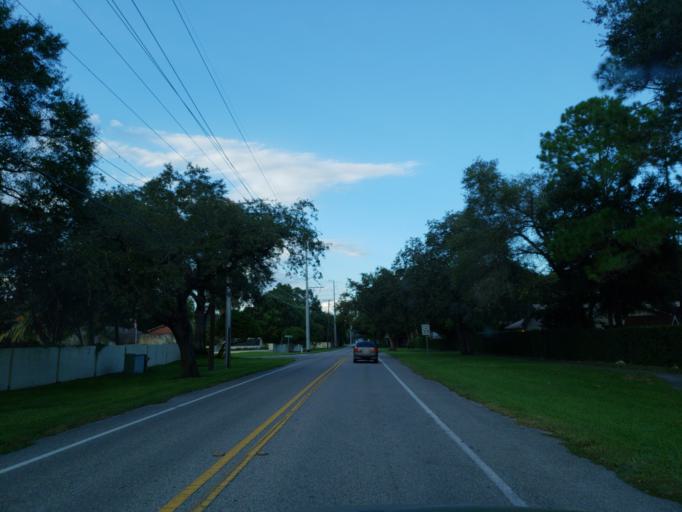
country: US
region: Florida
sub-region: Hillsborough County
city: Carrollwood Village
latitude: 28.0564
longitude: -82.5171
